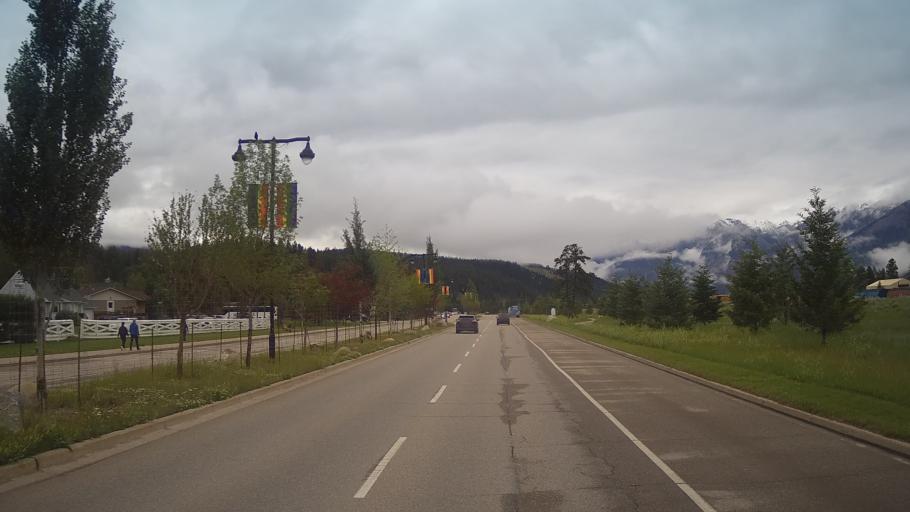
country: CA
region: Alberta
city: Jasper Park Lodge
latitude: 52.8844
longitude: -118.0776
